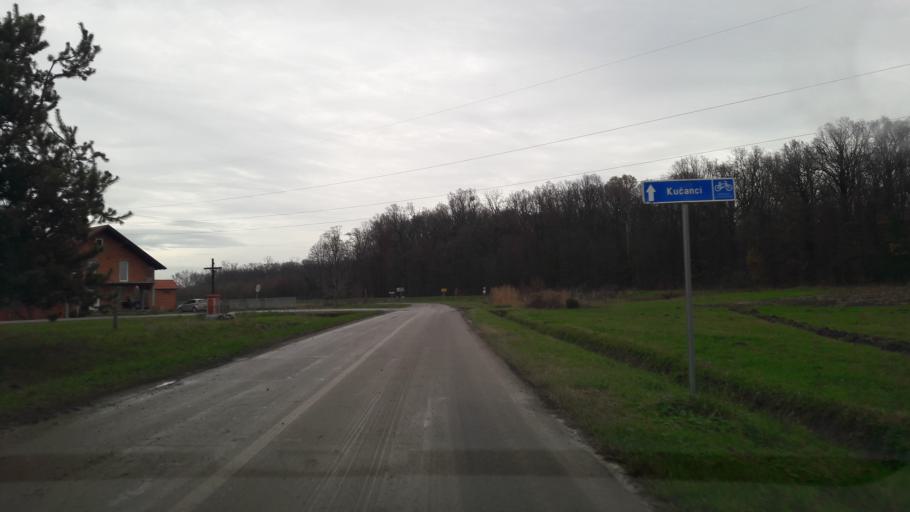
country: HR
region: Osjecko-Baranjska
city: Velimirovac
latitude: 45.6155
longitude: 18.0691
